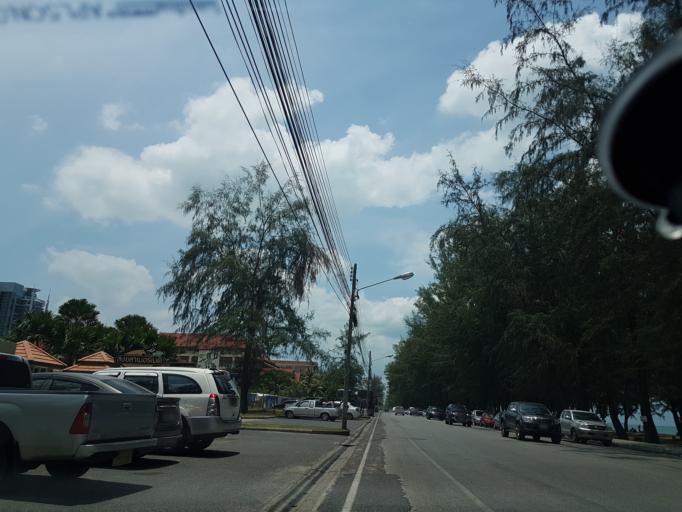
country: TH
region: Songkhla
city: Songkhla
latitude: 7.1989
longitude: 100.6053
